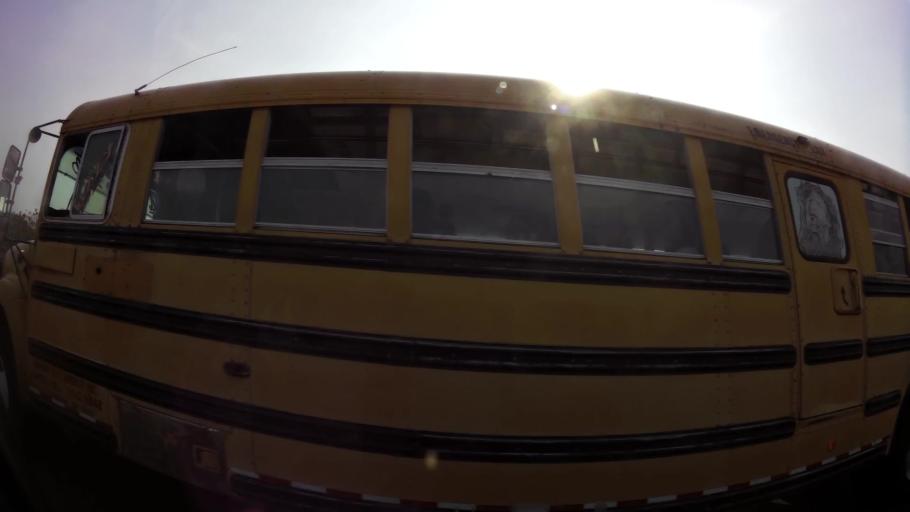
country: HN
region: Comayagua
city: Comayagua
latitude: 14.4124
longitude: -87.6232
